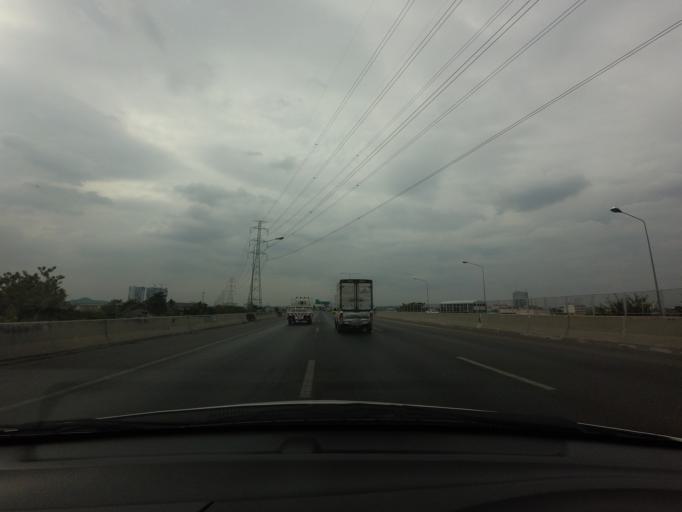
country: TH
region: Samut Prakan
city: Samut Prakan
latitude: 13.6230
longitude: 100.6032
